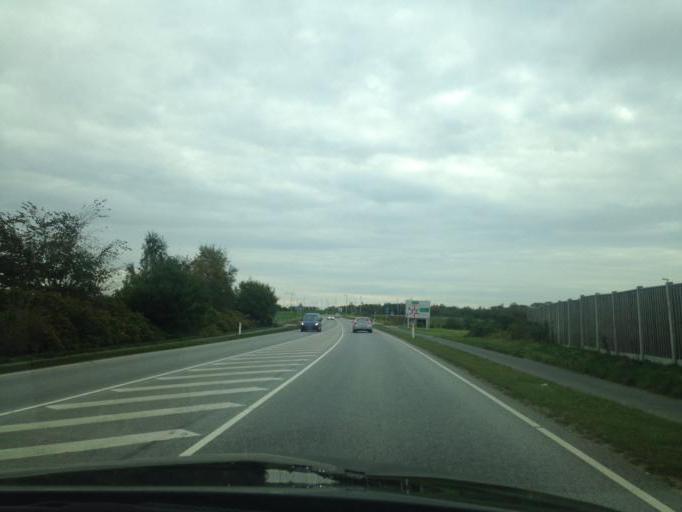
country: DK
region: South Denmark
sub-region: Haderslev Kommune
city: Vojens
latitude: 55.2458
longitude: 9.3946
